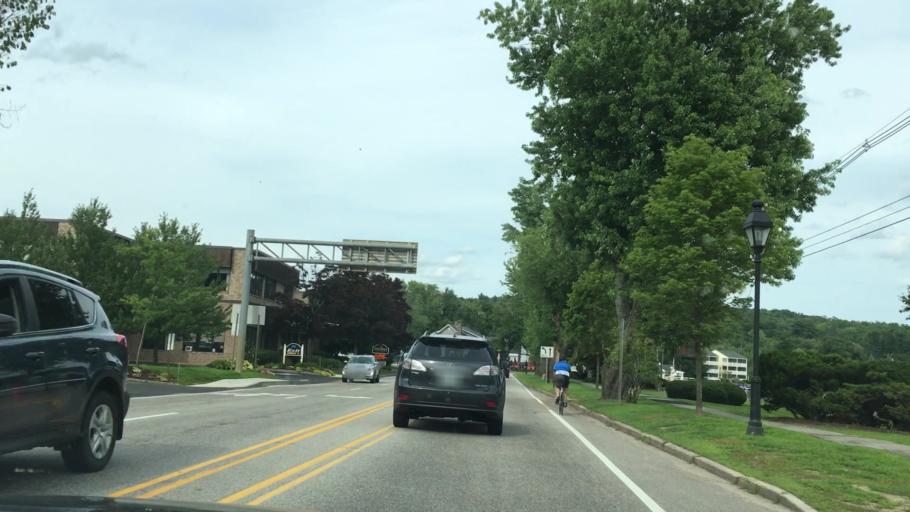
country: US
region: New Hampshire
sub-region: Belknap County
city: Meredith
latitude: 43.6586
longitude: -71.4989
